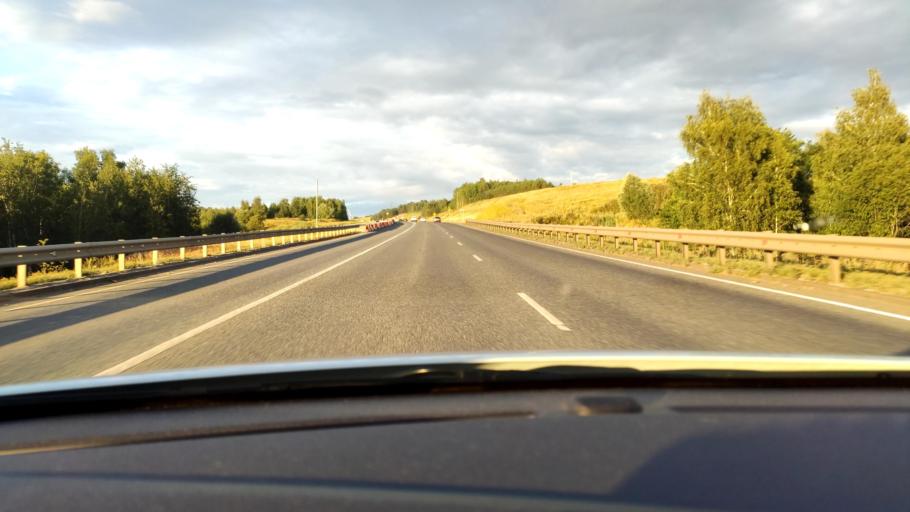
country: RU
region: Tatarstan
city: Sviyazhsk
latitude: 55.7160
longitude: 48.7222
